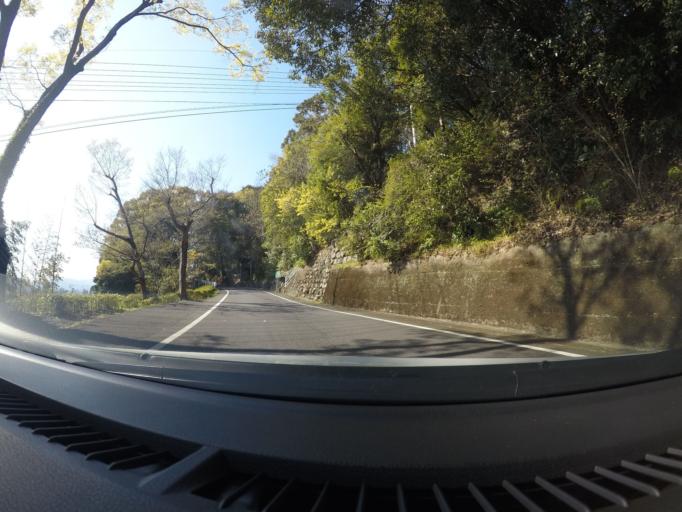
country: JP
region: Kochi
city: Kochi-shi
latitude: 33.5487
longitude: 133.5694
